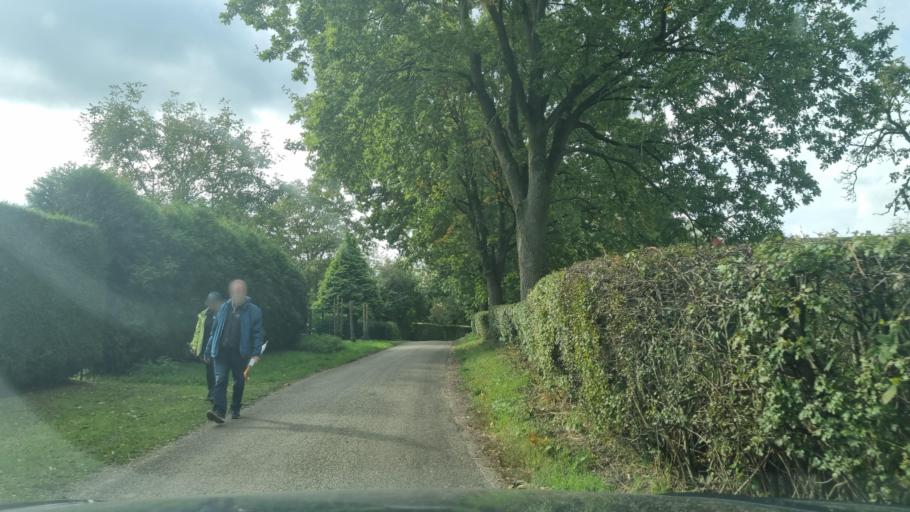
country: DE
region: North Rhine-Westphalia
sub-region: Regierungsbezirk Dusseldorf
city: Kleve
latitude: 51.7817
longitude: 6.0988
